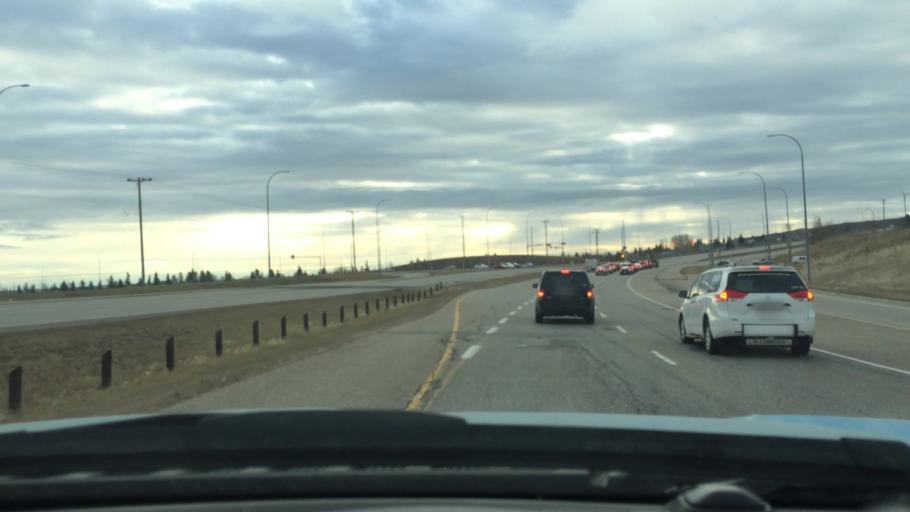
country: CA
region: Alberta
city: Calgary
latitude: 51.1441
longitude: -114.1262
